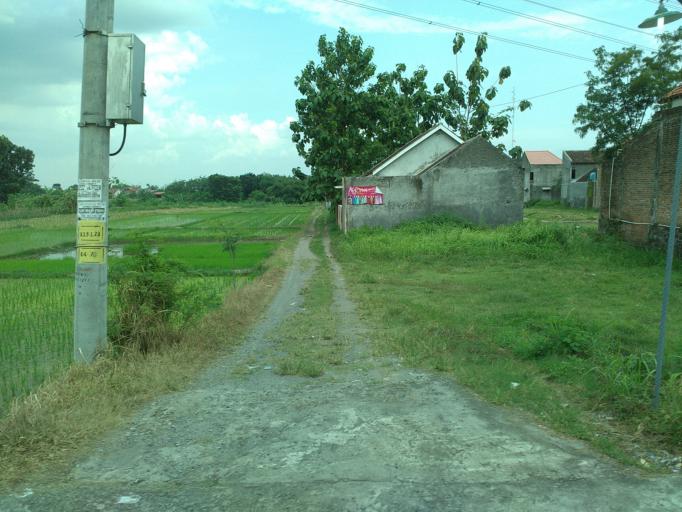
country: ID
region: Central Java
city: Karanganom
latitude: -7.6828
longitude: 110.6352
